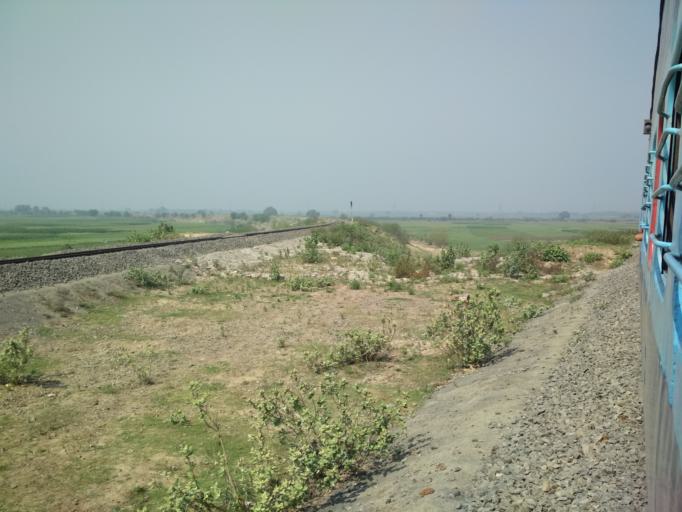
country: IN
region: Bihar
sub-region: Munger
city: Munger
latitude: 25.4403
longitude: 86.4302
